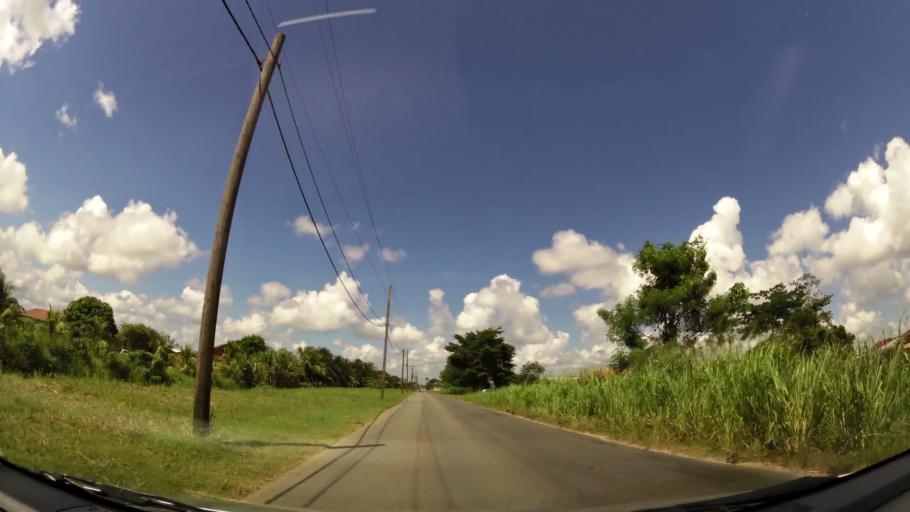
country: SR
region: Paramaribo
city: Paramaribo
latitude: 5.8611
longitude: -55.1278
